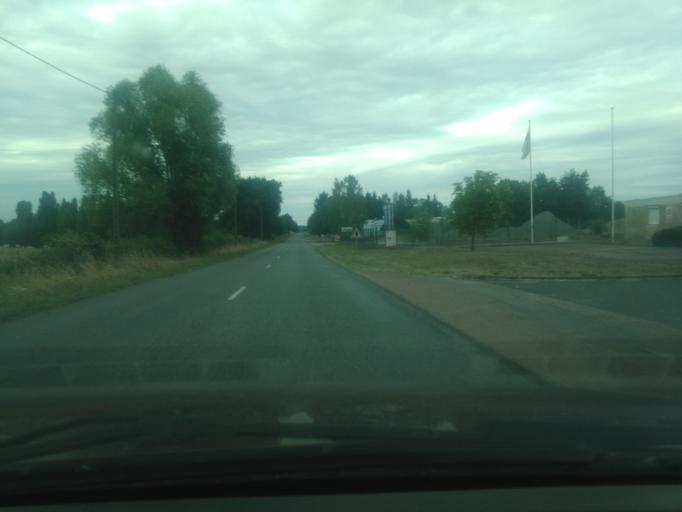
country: FR
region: Bourgogne
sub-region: Departement de la Nievre
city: Decize
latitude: 46.8040
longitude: 3.4461
